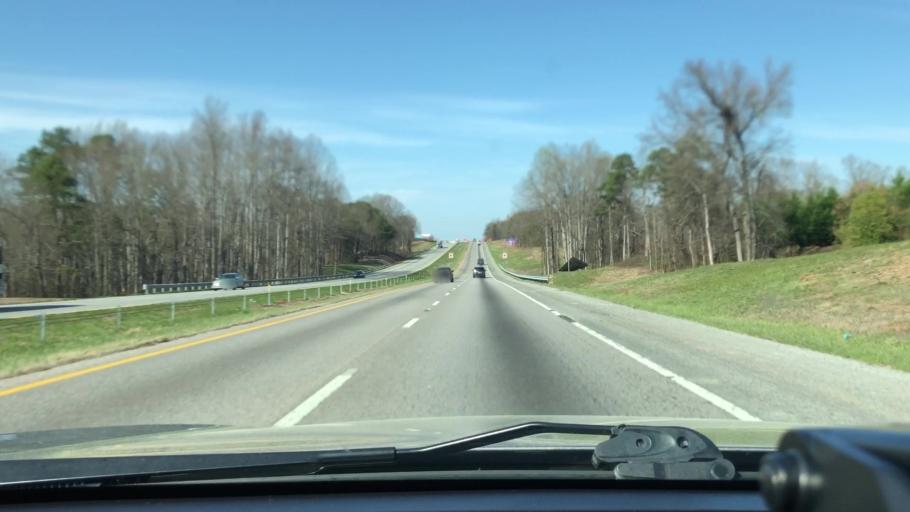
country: US
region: South Carolina
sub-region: Spartanburg County
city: Roebuck
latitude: 34.9050
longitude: -81.9910
